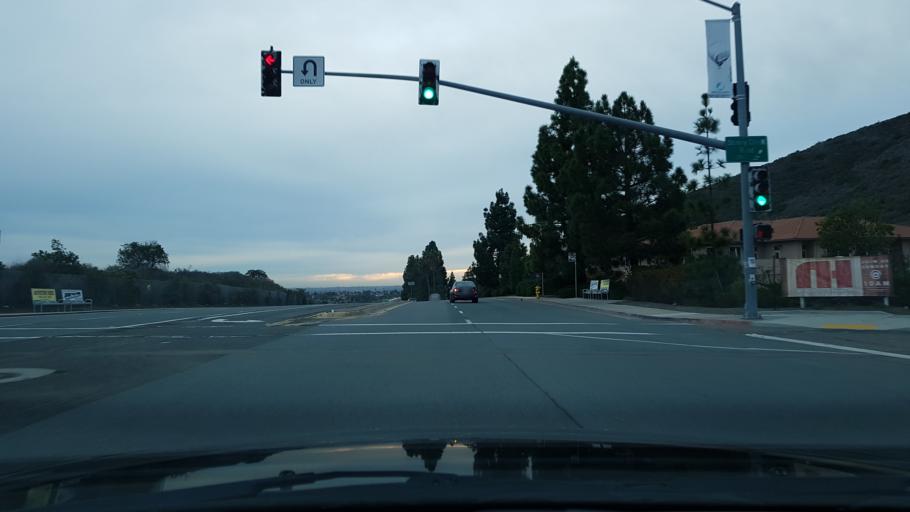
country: US
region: California
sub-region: San Diego County
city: Poway
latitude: 32.9637
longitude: -117.1029
